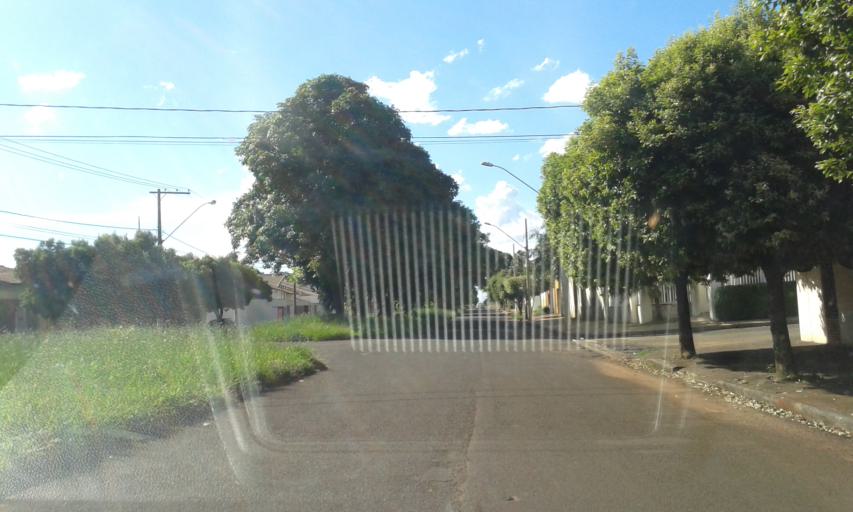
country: BR
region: Minas Gerais
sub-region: Ituiutaba
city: Ituiutaba
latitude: -18.9696
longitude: -49.4489
